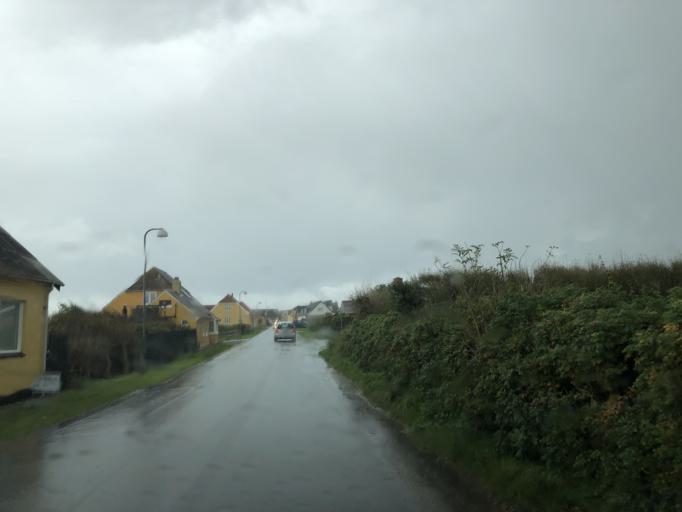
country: DK
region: Central Jutland
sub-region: Lemvig Kommune
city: Harboore
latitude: 56.5275
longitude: 8.1251
